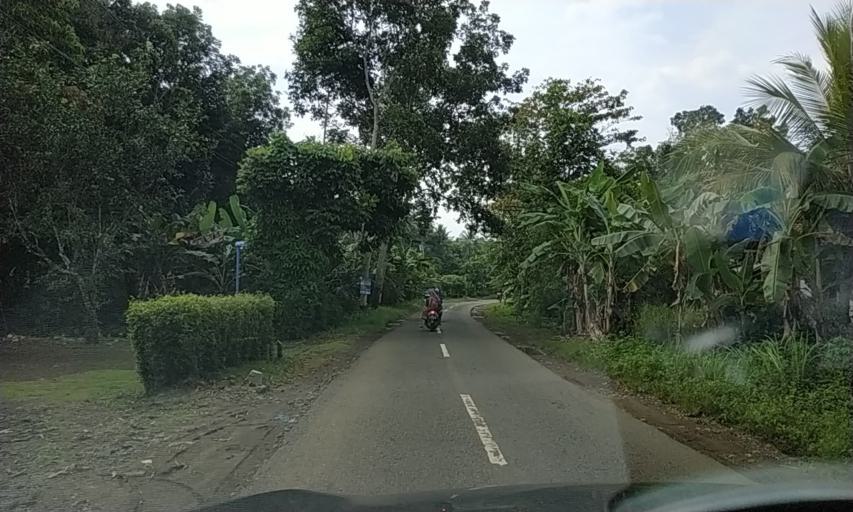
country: ID
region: Central Java
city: Meluwung
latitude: -7.3814
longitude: 108.7002
